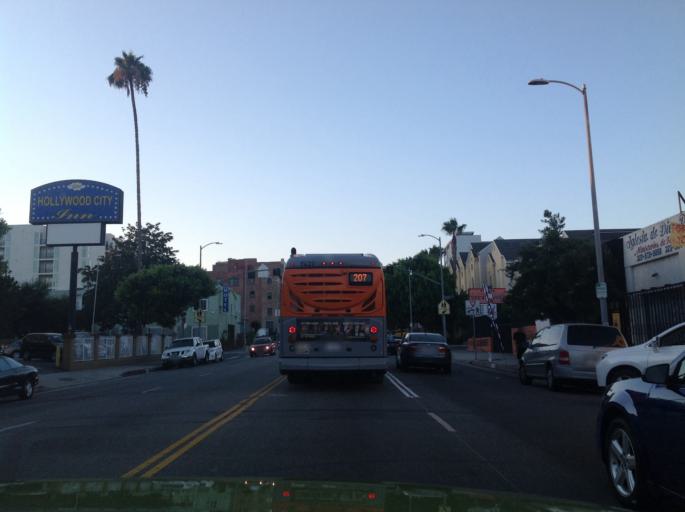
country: US
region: California
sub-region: Los Angeles County
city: Hollywood
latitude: 34.0999
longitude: -118.3092
